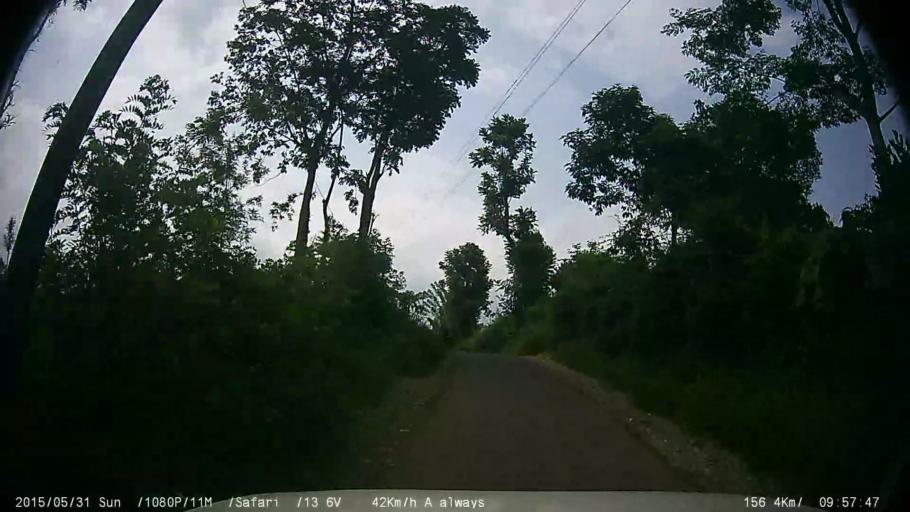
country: IN
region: Kerala
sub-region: Wayanad
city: Kalpetta
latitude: 11.5929
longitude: 76.0594
